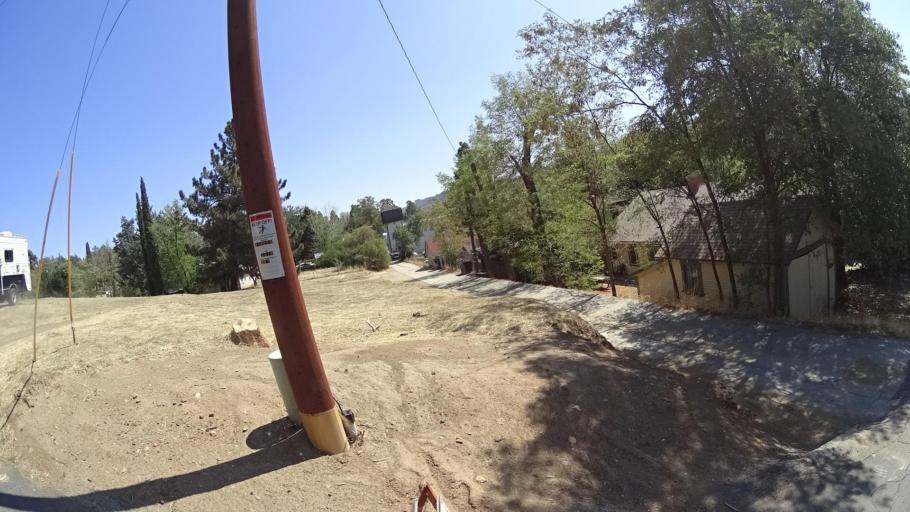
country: US
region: California
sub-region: San Diego County
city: Julian
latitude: 33.0796
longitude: -116.6030
